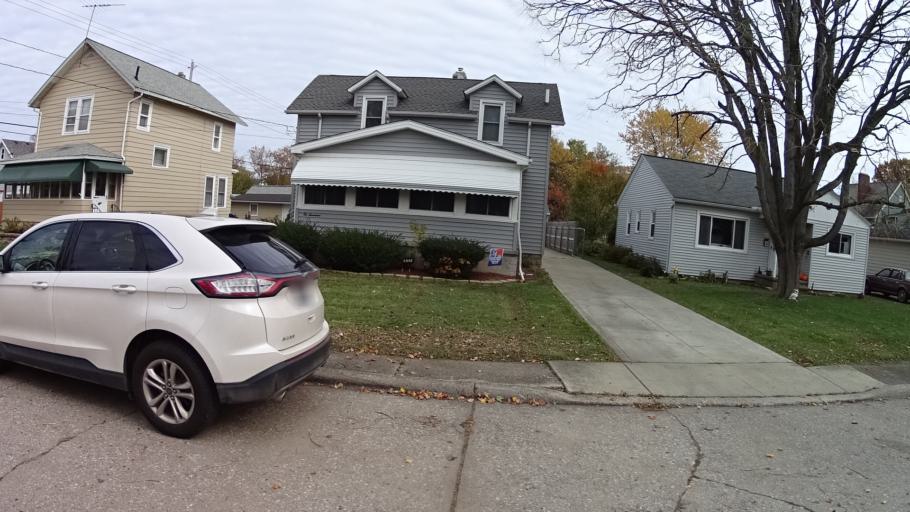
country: US
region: Ohio
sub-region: Lorain County
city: Lorain
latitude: 41.4749
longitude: -82.1577
